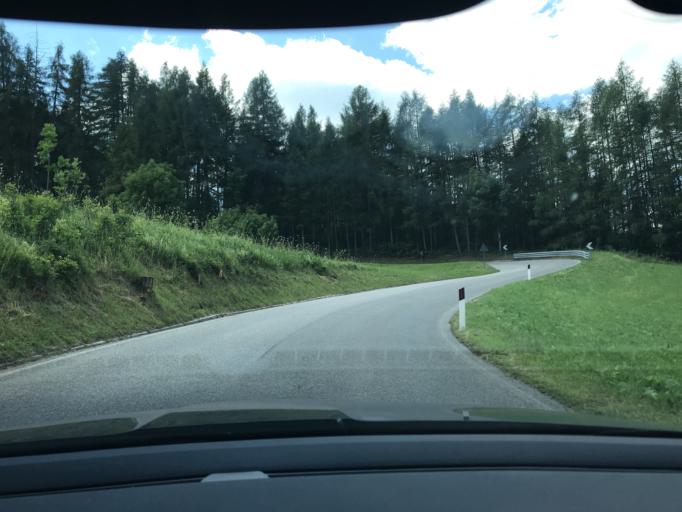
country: IT
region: Veneto
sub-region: Provincia di Belluno
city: Cortina d'Ampezzo
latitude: 46.5426
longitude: 12.1555
